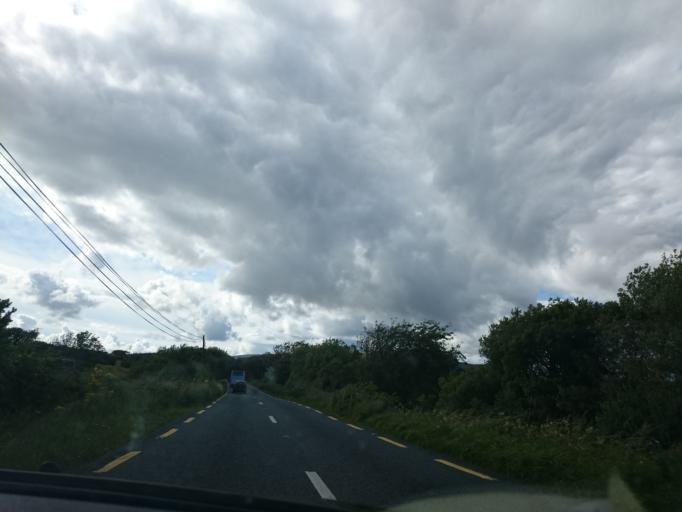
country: IE
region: Connaught
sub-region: Maigh Eo
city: Westport
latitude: 53.8996
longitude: -9.5647
